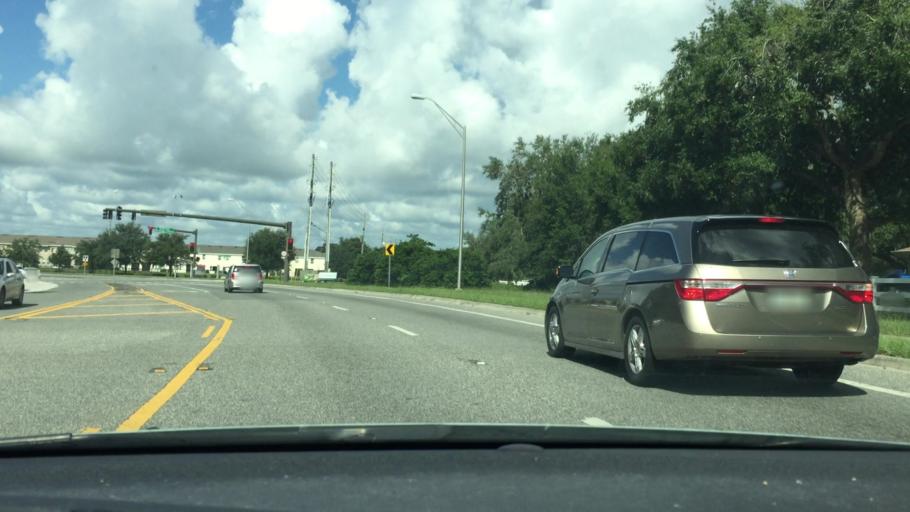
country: US
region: Florida
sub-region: Osceola County
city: Buenaventura Lakes
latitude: 28.3042
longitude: -81.3703
